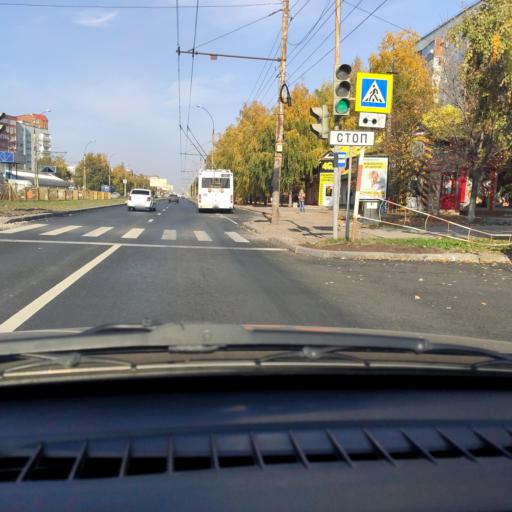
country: RU
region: Samara
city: Tol'yatti
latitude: 53.5293
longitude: 49.3277
